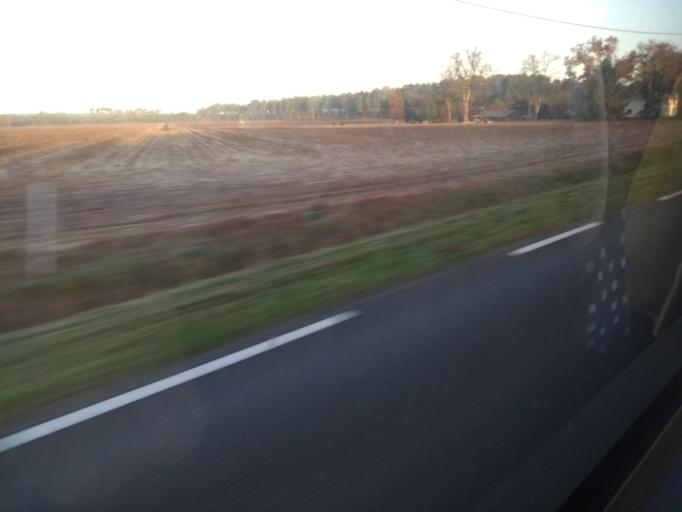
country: FR
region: Aquitaine
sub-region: Departement de la Gironde
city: Le Barp
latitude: 44.5878
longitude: -0.7754
